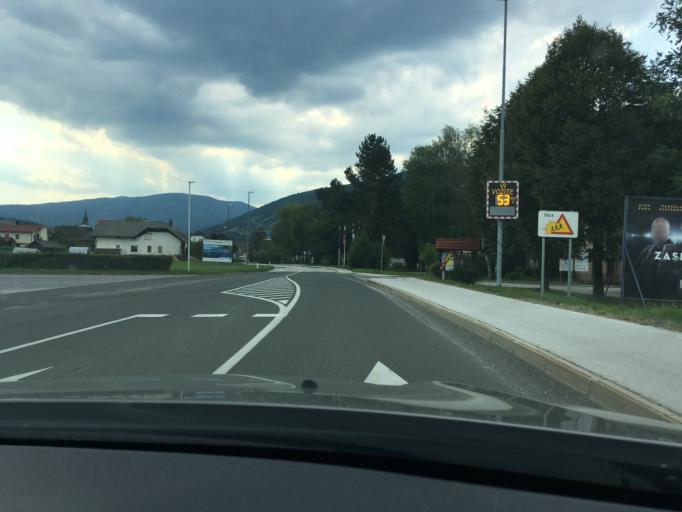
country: SI
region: Straza
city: Straza
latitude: 45.7825
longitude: 15.0830
